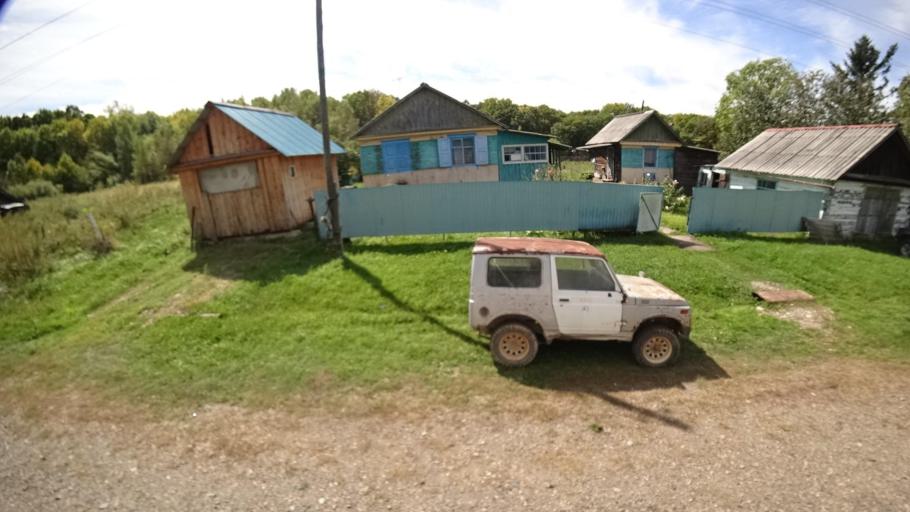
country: RU
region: Primorskiy
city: Yakovlevka
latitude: 44.6531
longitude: 133.7479
